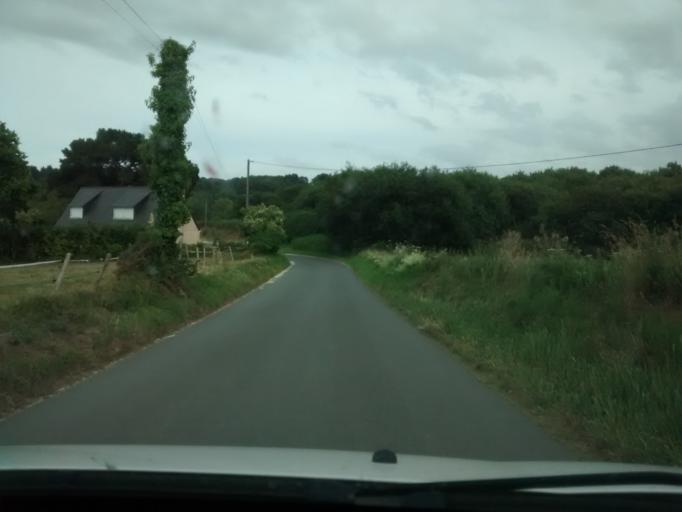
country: FR
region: Brittany
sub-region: Departement des Cotes-d'Armor
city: Penvenan
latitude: 48.8342
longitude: -3.2707
